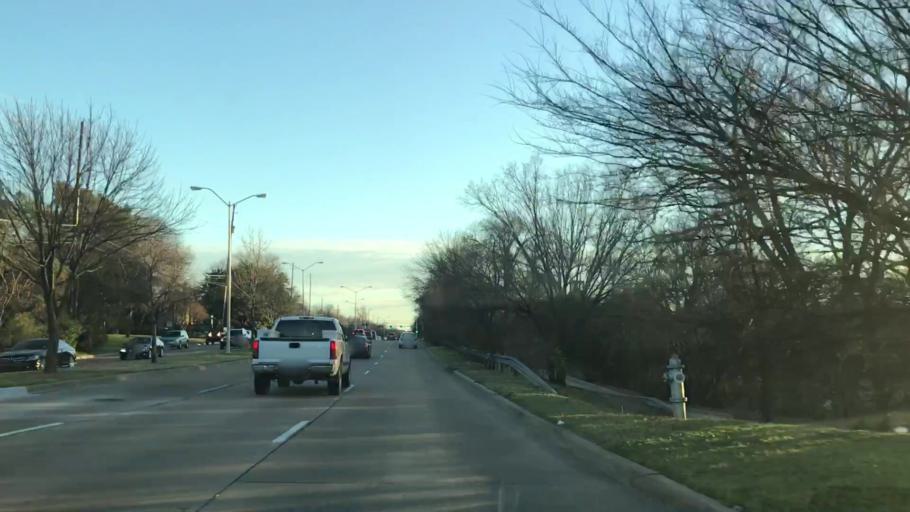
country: US
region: Texas
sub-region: Dallas County
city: Addison
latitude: 32.9358
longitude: -96.7863
